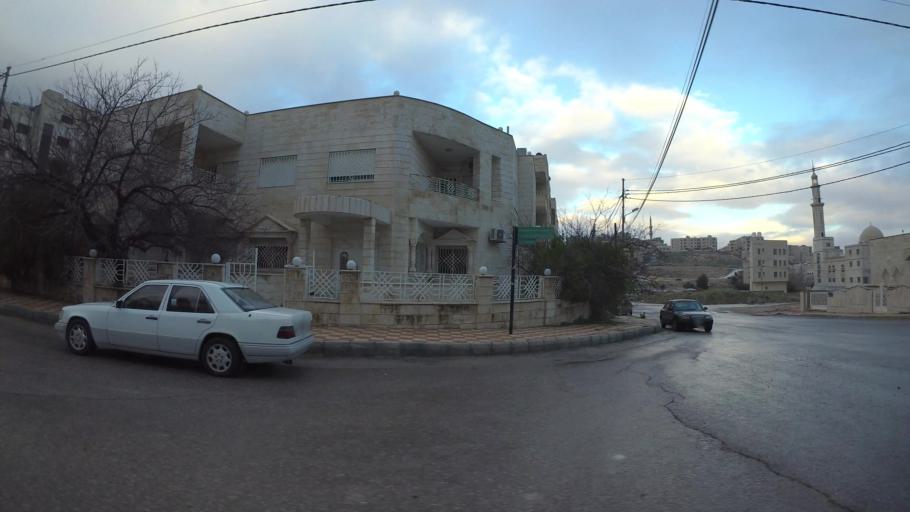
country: JO
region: Amman
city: Amman
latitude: 31.9904
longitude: 35.9160
